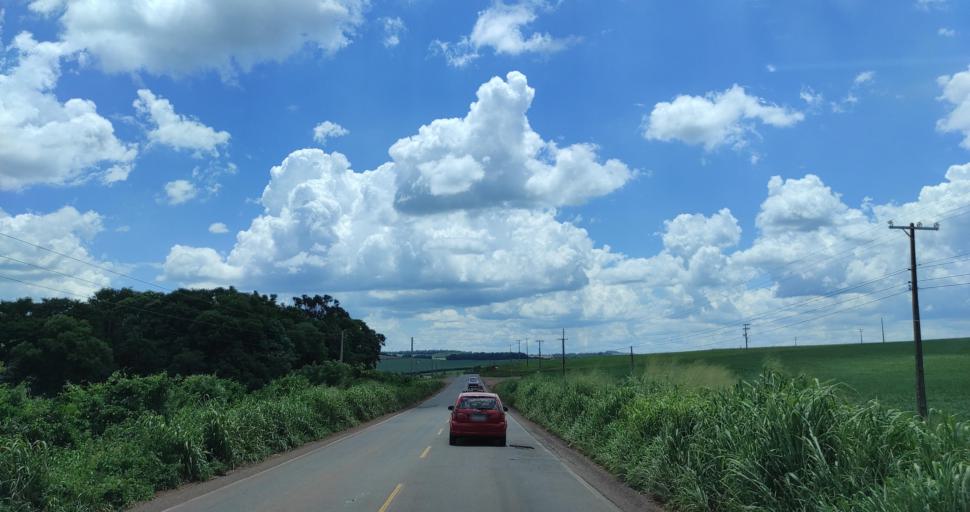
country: BR
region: Santa Catarina
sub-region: Xanxere
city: Xanxere
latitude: -26.7573
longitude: -52.4031
